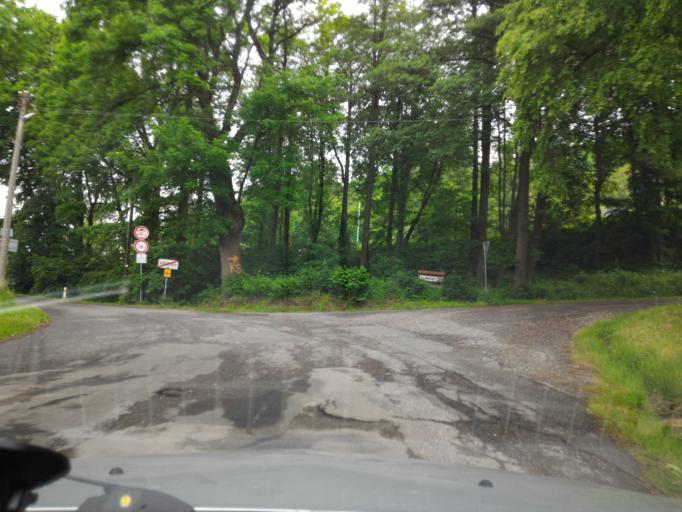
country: CZ
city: Osecna
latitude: 50.7510
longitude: 14.9175
